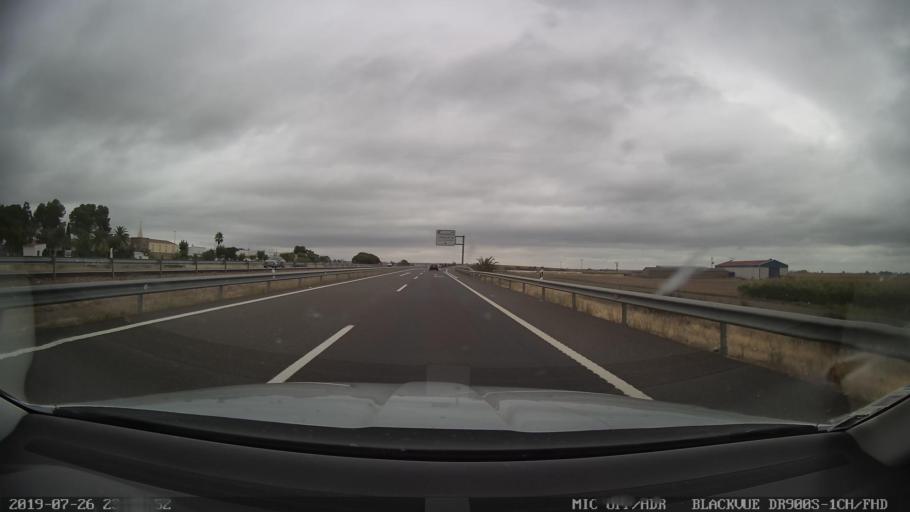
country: ES
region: Extremadura
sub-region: Provincia de Badajoz
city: Santa Amalia
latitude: 39.0735
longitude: -6.0368
